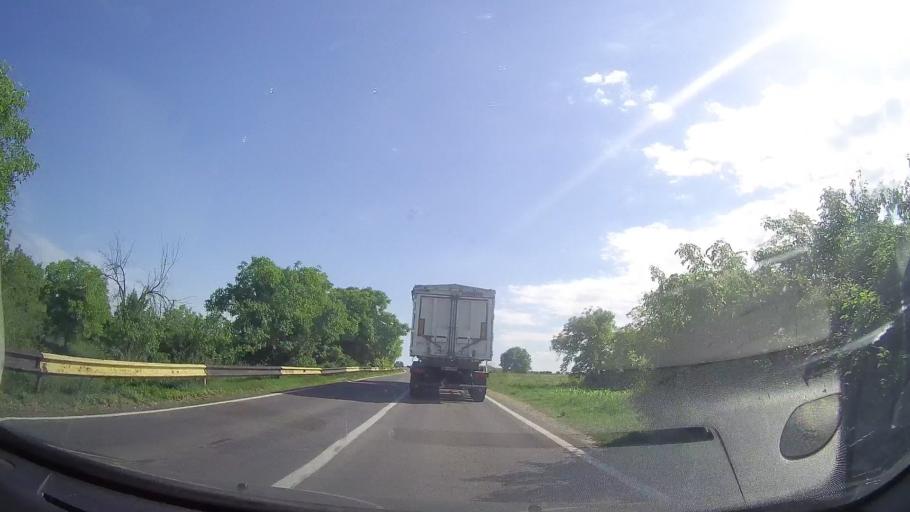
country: RO
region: Prahova
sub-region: Comuna Izvoarele
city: Homoraciu
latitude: 45.2484
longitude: 26.0238
